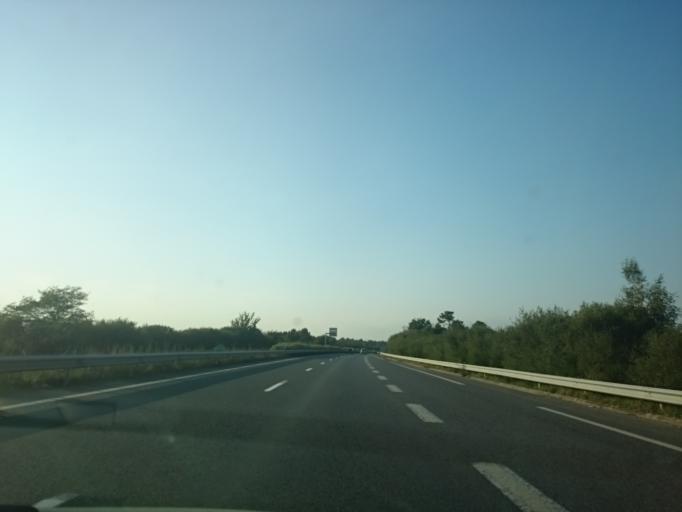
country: FR
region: Brittany
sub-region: Departement du Morbihan
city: Nivillac
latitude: 47.5032
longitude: -2.2668
